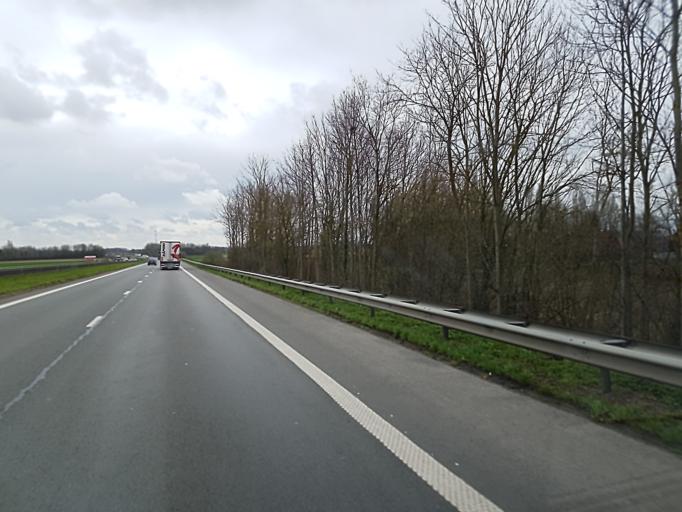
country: BE
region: Wallonia
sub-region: Province du Hainaut
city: Estaimpuis
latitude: 50.6692
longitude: 3.2883
